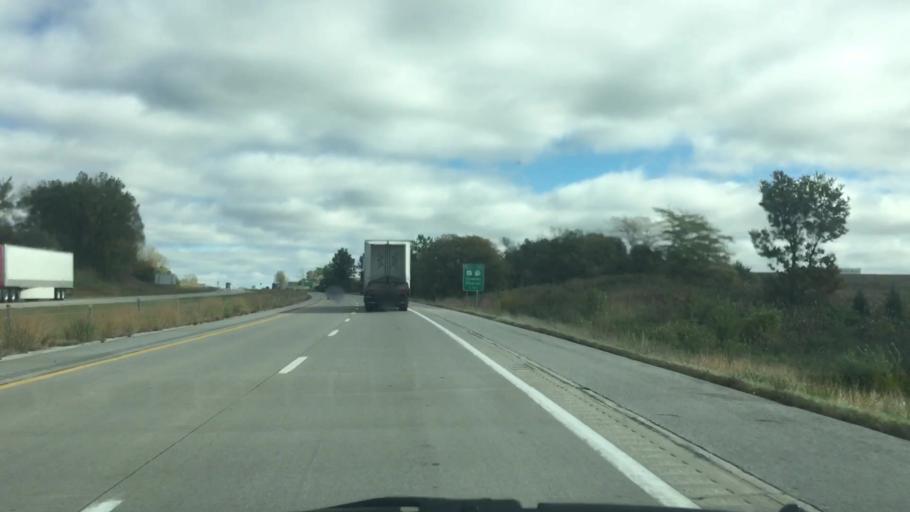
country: US
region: Iowa
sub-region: Jasper County
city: Newton
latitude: 41.6808
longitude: -93.0976
